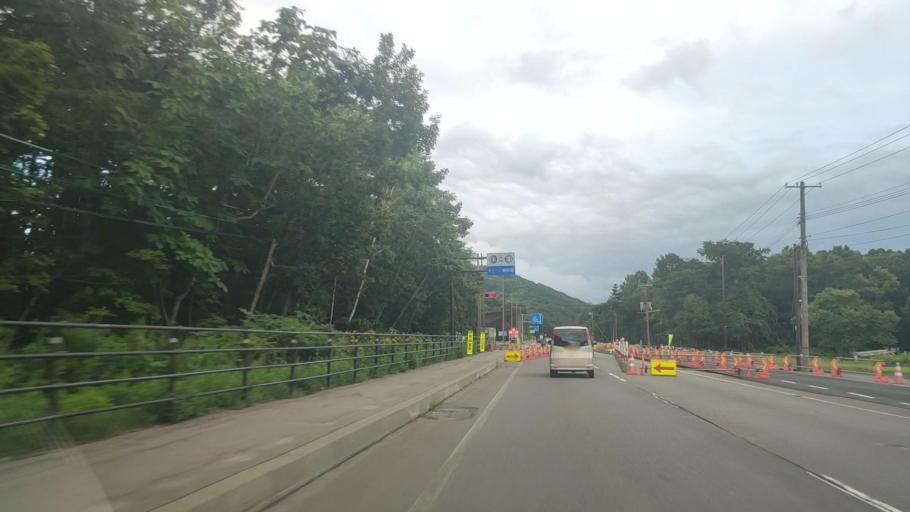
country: JP
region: Hokkaido
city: Nanae
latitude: 41.9932
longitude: 140.6370
